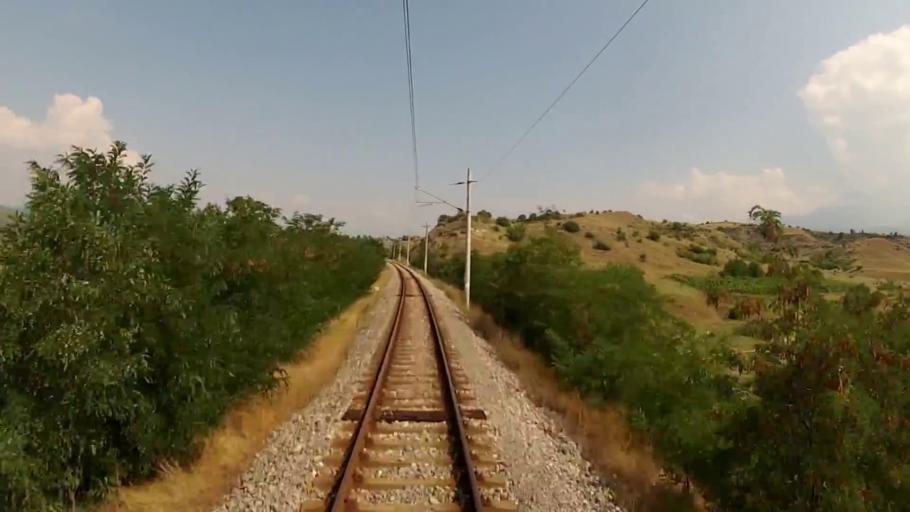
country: BG
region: Blagoevgrad
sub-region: Obshtina Sandanski
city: Sandanski
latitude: 41.5885
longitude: 23.2365
